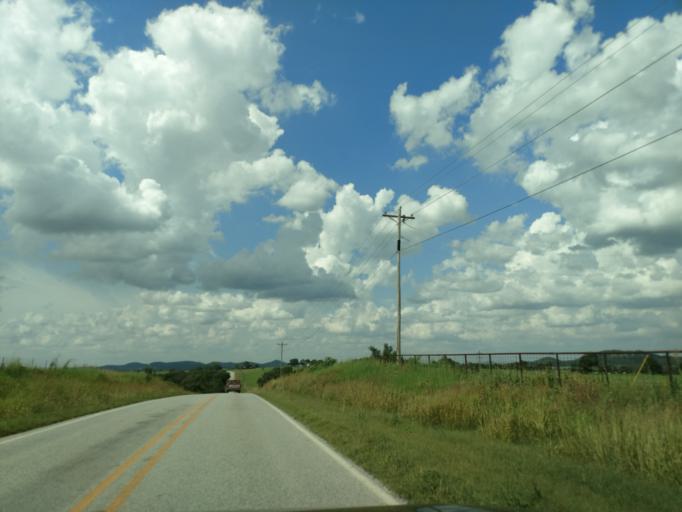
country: US
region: Arkansas
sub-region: Carroll County
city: Berryville
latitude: 36.4595
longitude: -93.5558
